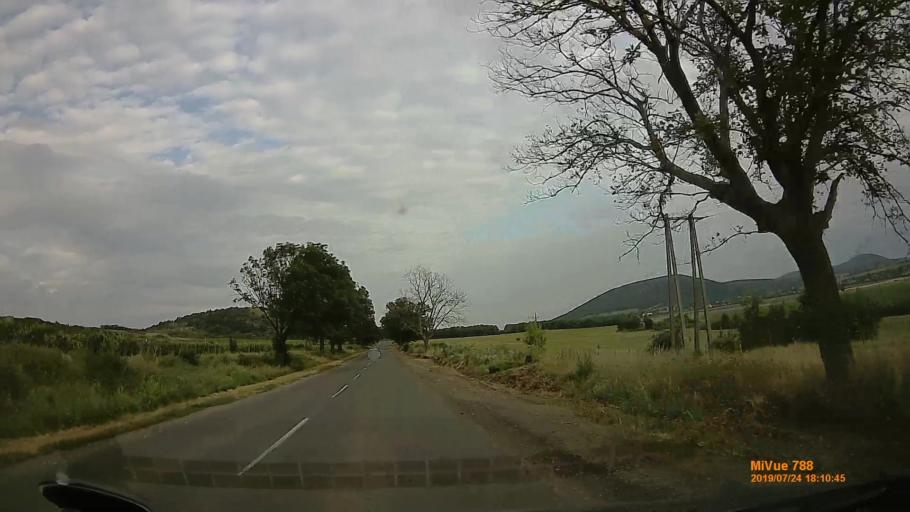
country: HU
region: Borsod-Abauj-Zemplen
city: Abaujszanto
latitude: 48.2565
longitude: 21.1922
